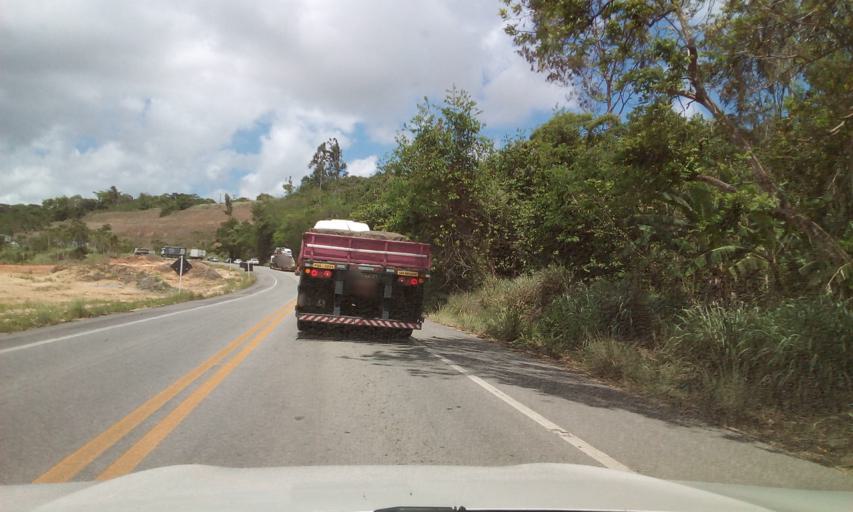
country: BR
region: Alagoas
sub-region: Pilar
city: Pilar
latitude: -9.5942
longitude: -36.0035
